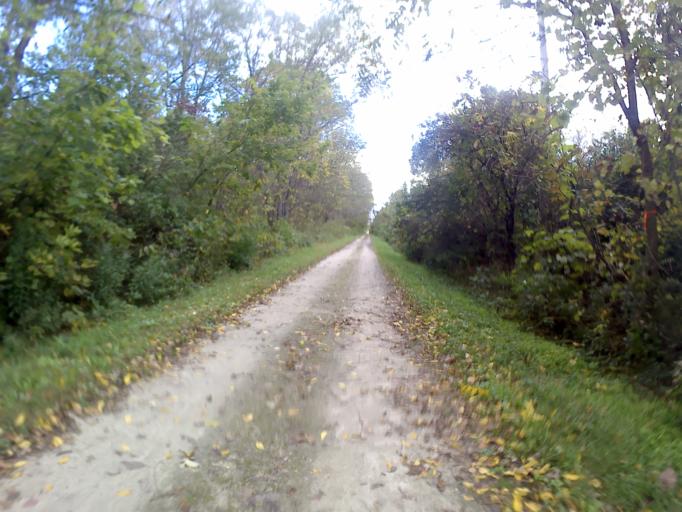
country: US
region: Illinois
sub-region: DuPage County
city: Wayne
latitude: 41.9701
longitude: -88.2624
